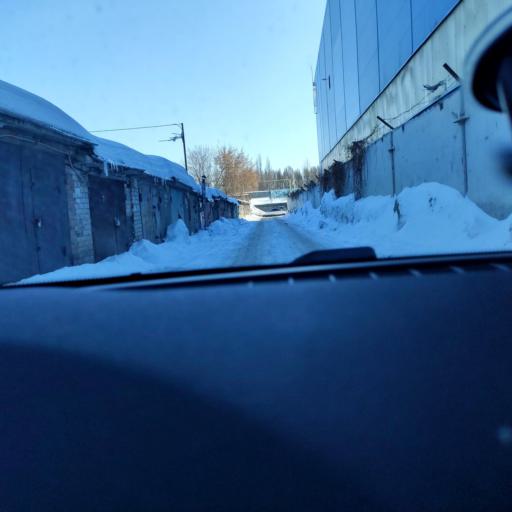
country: RU
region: Samara
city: Petra-Dubrava
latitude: 53.2511
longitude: 50.3069
